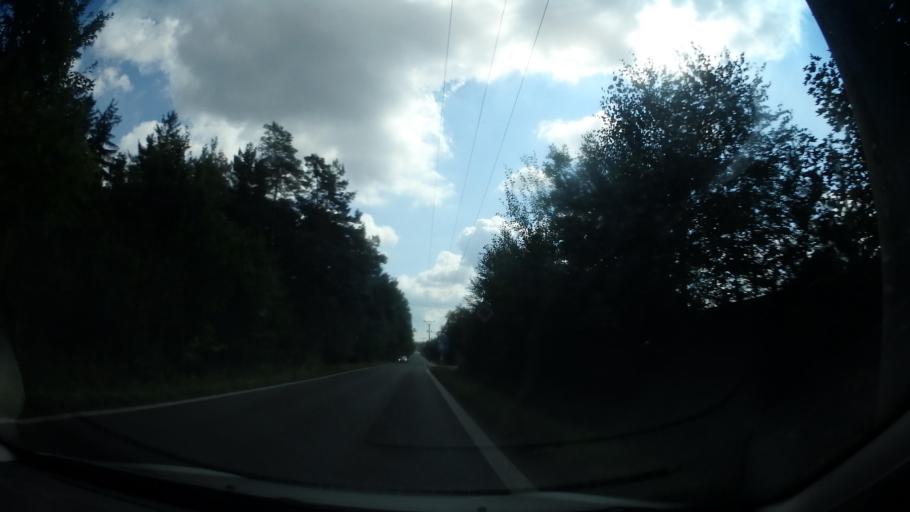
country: CZ
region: Central Bohemia
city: Mukarov
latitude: 49.9593
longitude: 14.7482
